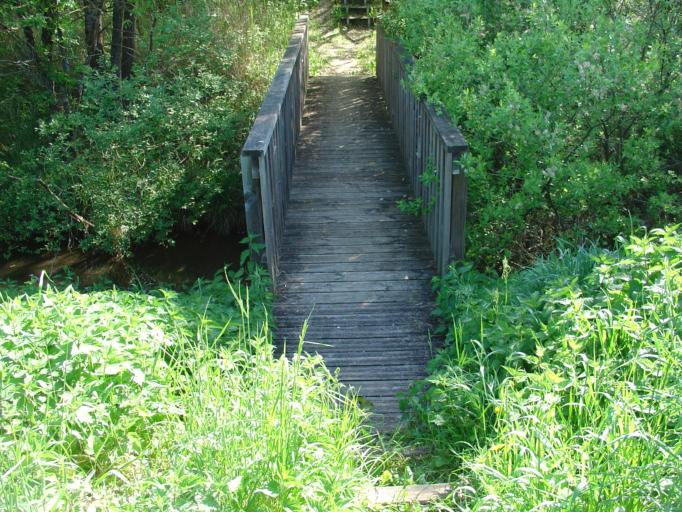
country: FR
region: Lorraine
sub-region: Departement de Meurthe-et-Moselle
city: Foug
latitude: 48.6893
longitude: 5.7591
